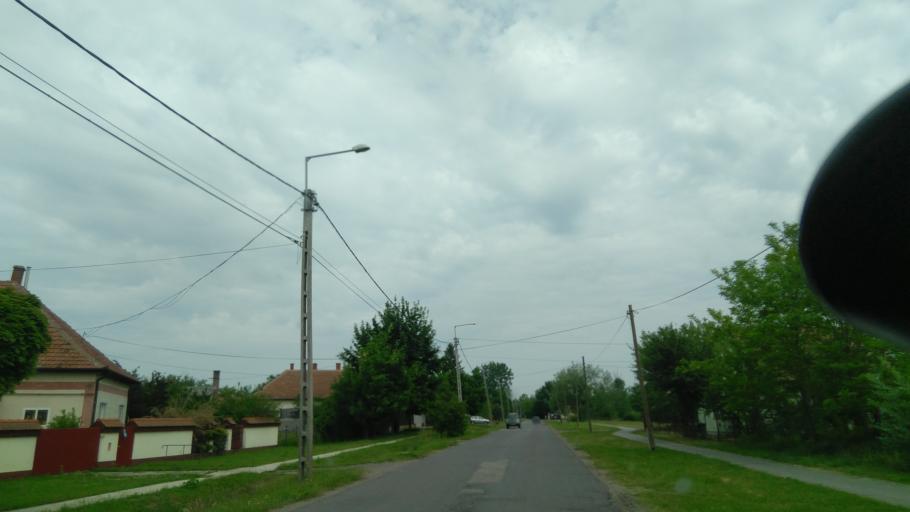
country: HU
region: Bekes
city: Szeghalom
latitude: 47.0309
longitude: 21.1669
